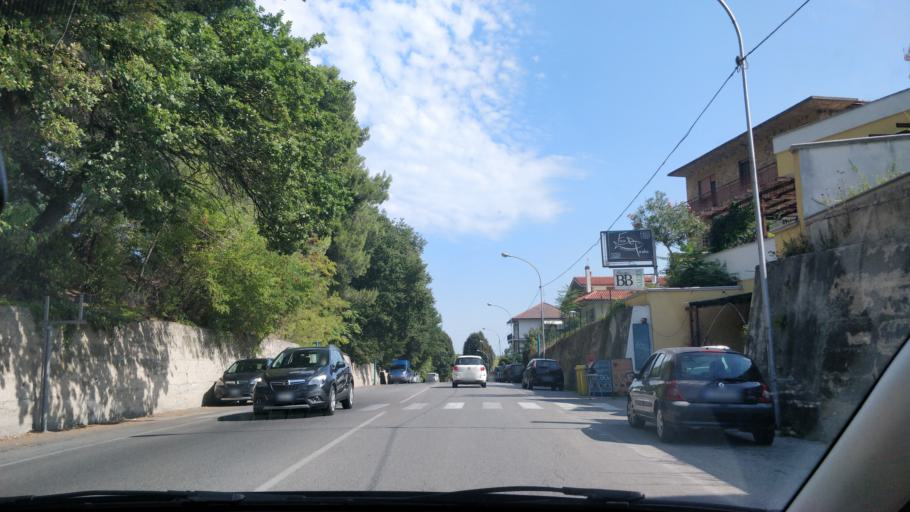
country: IT
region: Abruzzo
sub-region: Provincia di Chieti
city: Chieti
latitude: 42.3874
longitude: 14.1563
